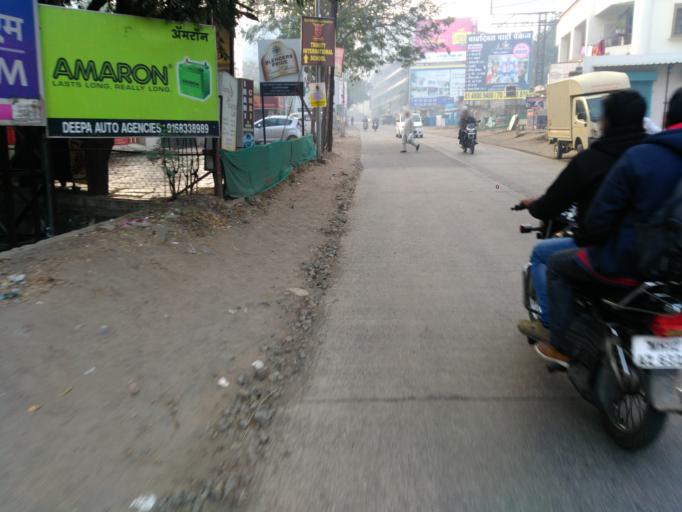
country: IN
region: Maharashtra
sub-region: Pune Division
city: Pune
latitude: 18.4576
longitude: 73.9125
